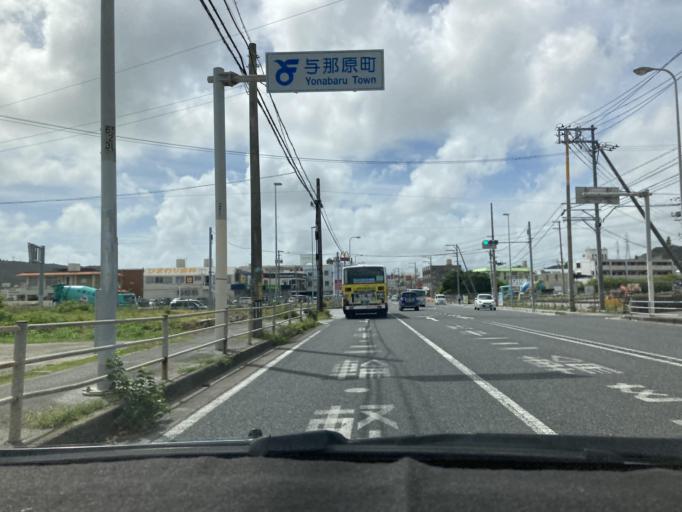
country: JP
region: Okinawa
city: Ginowan
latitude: 26.2126
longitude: 127.7607
